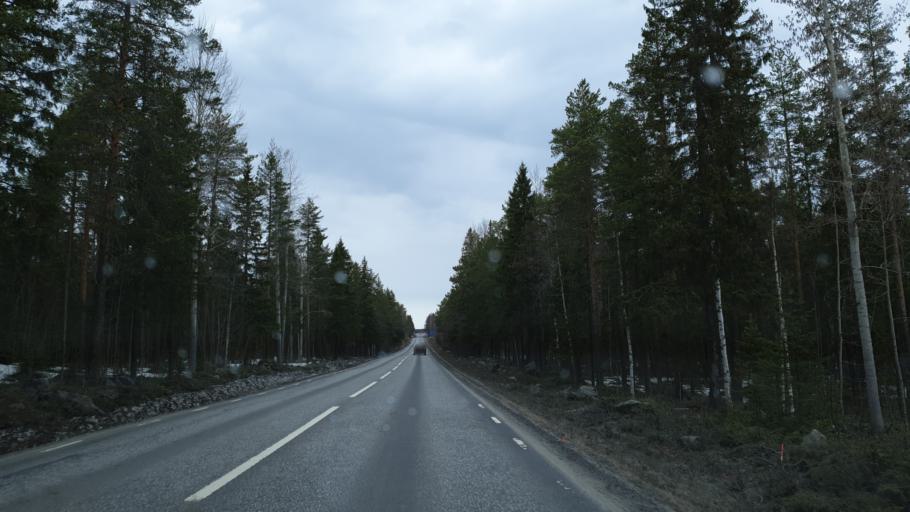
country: SE
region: Vaesterbotten
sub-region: Skelleftea Kommun
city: Viken
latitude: 64.6566
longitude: 20.9536
